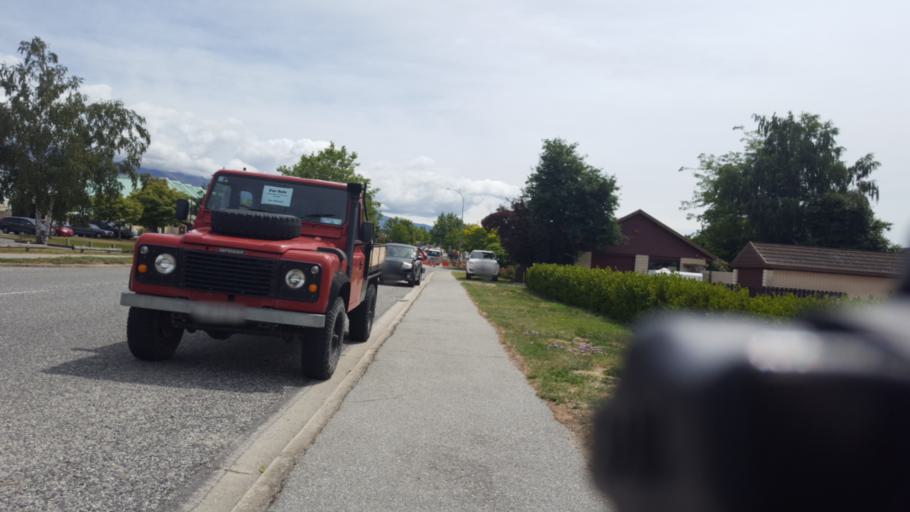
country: NZ
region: Otago
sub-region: Queenstown-Lakes District
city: Wanaka
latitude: -45.0401
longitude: 169.1978
